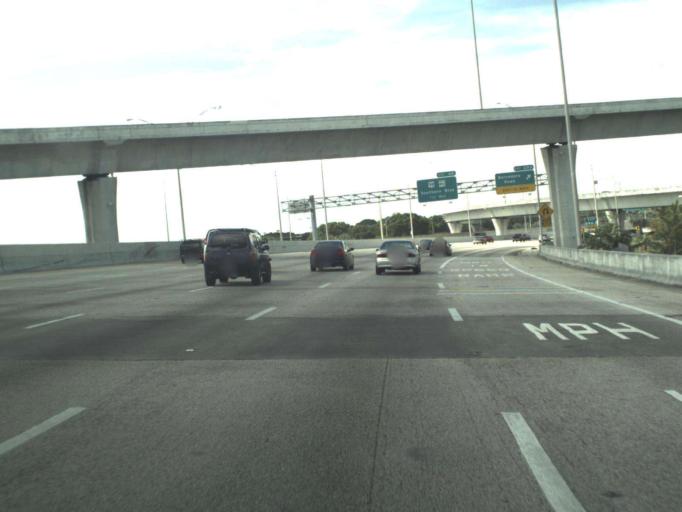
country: US
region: Florida
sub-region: Palm Beach County
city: West Palm Beach
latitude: 26.6910
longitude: -80.0671
